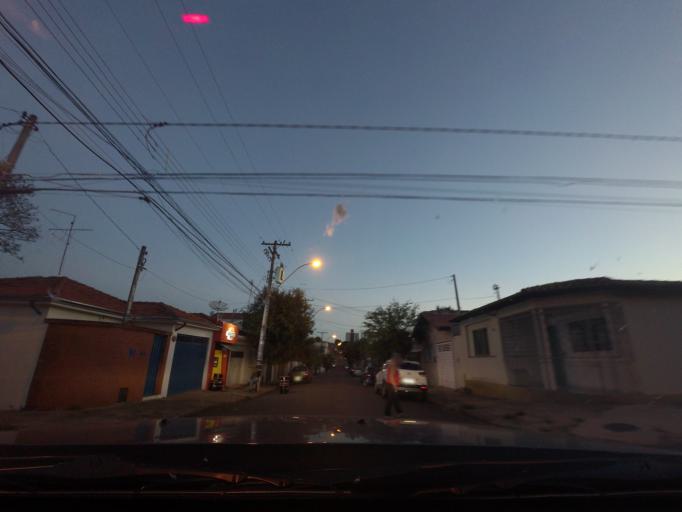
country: BR
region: Sao Paulo
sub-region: Piracicaba
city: Piracicaba
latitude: -22.7162
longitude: -47.6317
